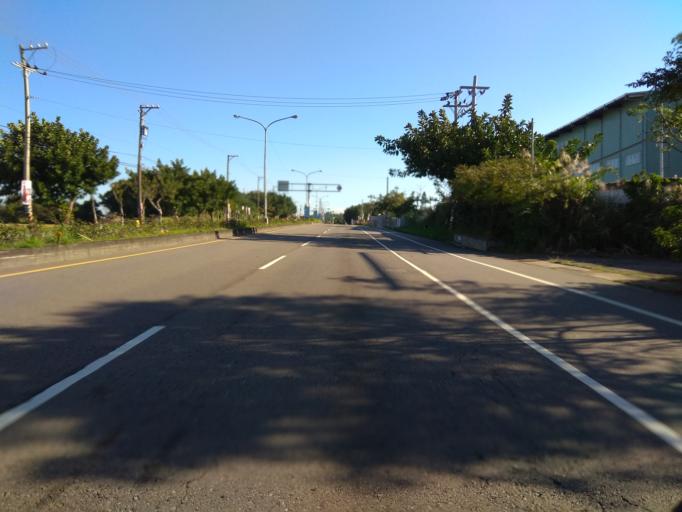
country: TW
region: Taiwan
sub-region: Hsinchu
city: Zhubei
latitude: 24.8823
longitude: 121.0716
